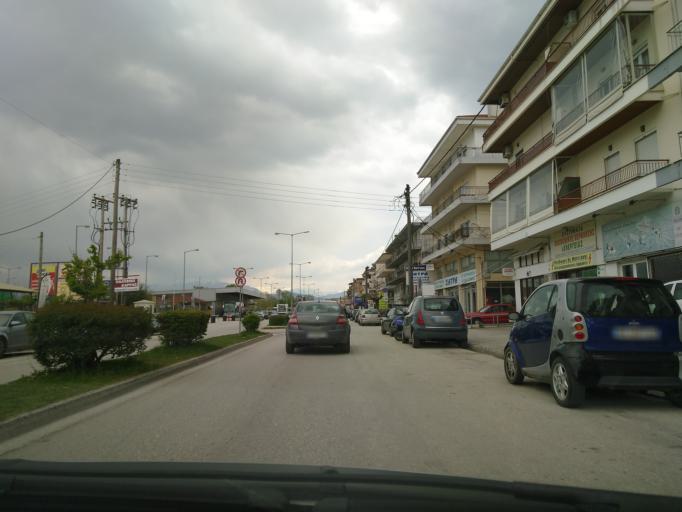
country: GR
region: Epirus
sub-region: Nomos Ioanninon
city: Ioannina
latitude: 39.6751
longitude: 20.8454
